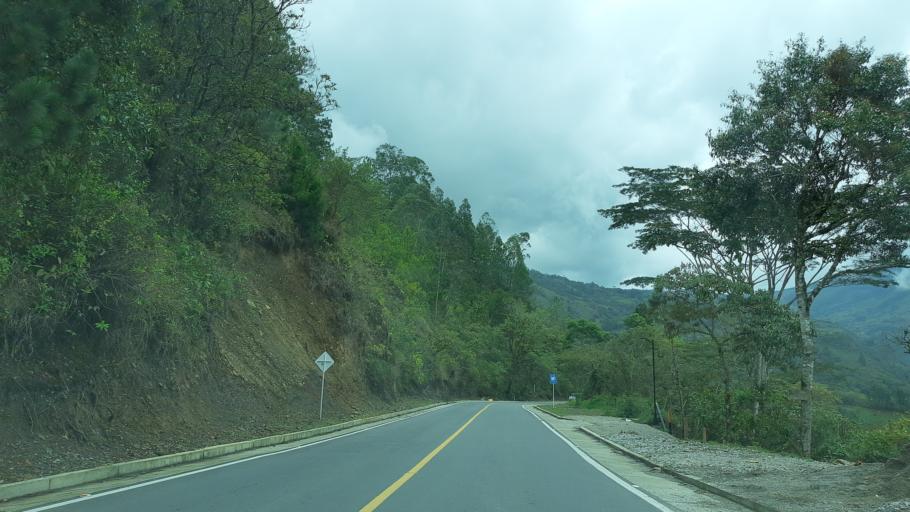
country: CO
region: Boyaca
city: Chivor
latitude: 4.9560
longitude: -73.3191
